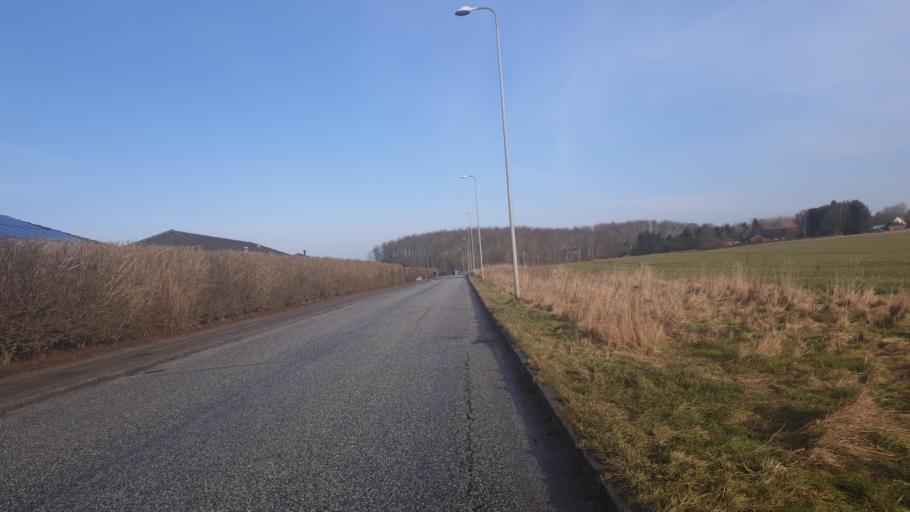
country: DK
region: Central Jutland
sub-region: Hedensted Kommune
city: Hedensted
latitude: 55.7702
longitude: 9.7200
